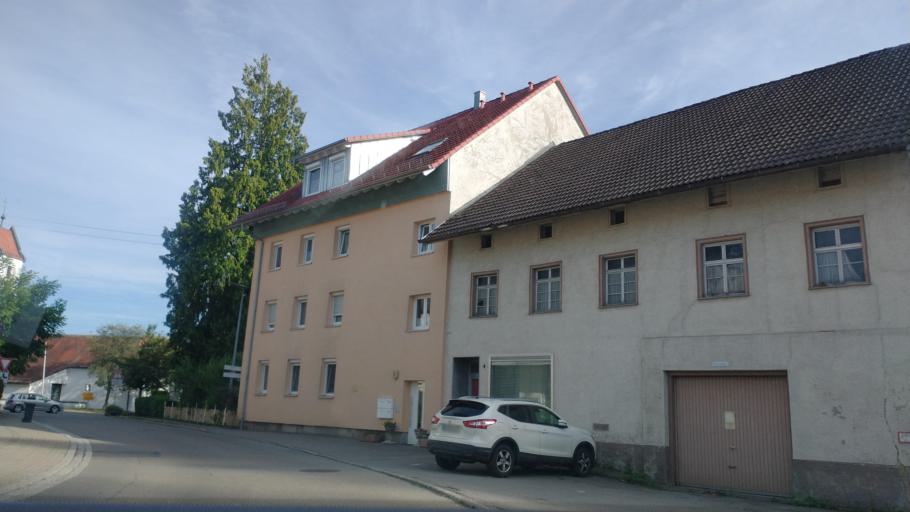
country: DE
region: Baden-Wuerttemberg
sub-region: Tuebingen Region
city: Neukirch
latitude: 47.6585
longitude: 9.7020
